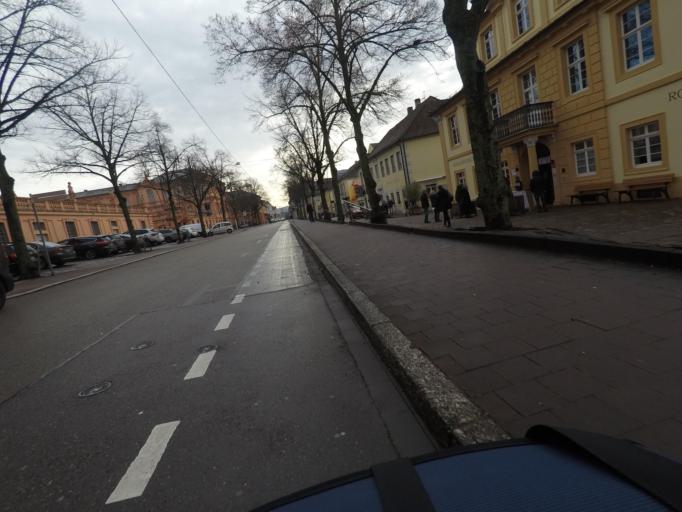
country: DE
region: Baden-Wuerttemberg
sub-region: Karlsruhe Region
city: Rastatt
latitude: 48.8589
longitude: 8.2035
